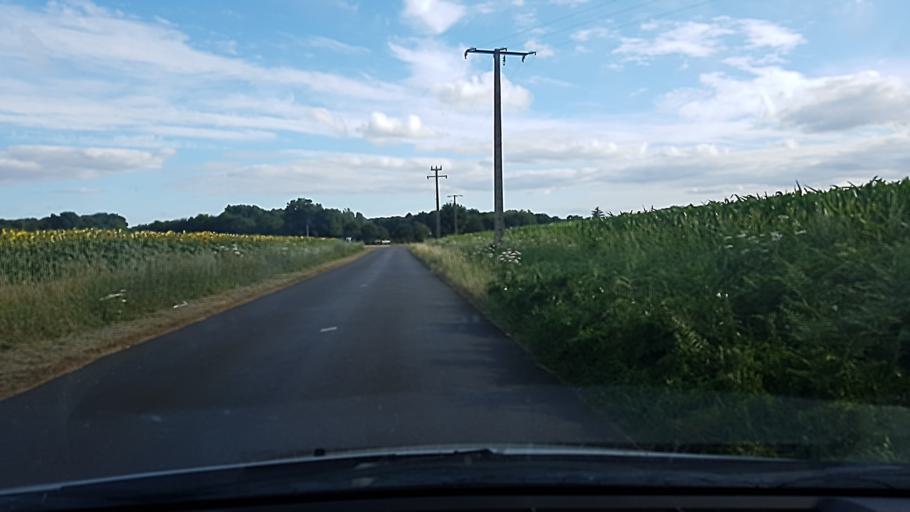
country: FR
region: Pays de la Loire
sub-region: Departement de Maine-et-Loire
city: Jarze
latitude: 47.5215
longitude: -0.2128
